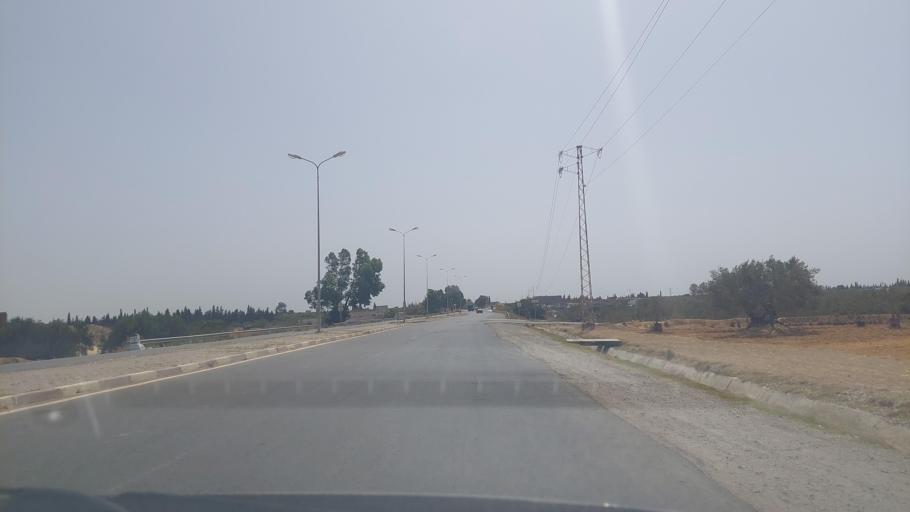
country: TN
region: Al Munastir
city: Qasr Hallal
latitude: 35.6295
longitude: 10.8717
